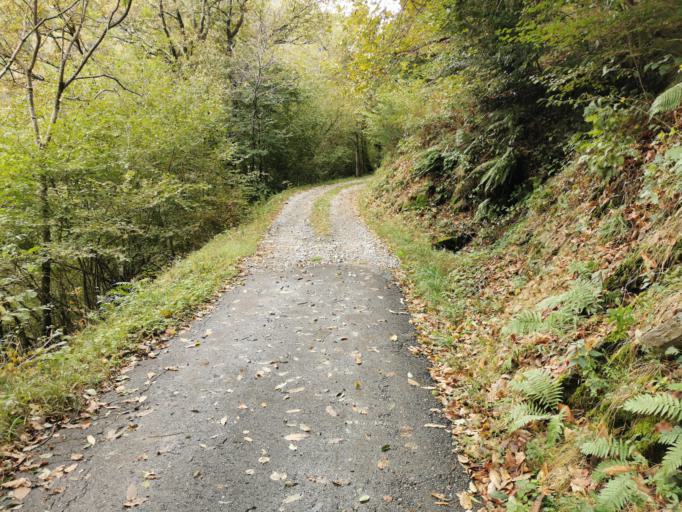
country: CH
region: Ticino
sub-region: Bellinzona District
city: Cadenazzo
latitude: 46.1233
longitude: 8.9796
